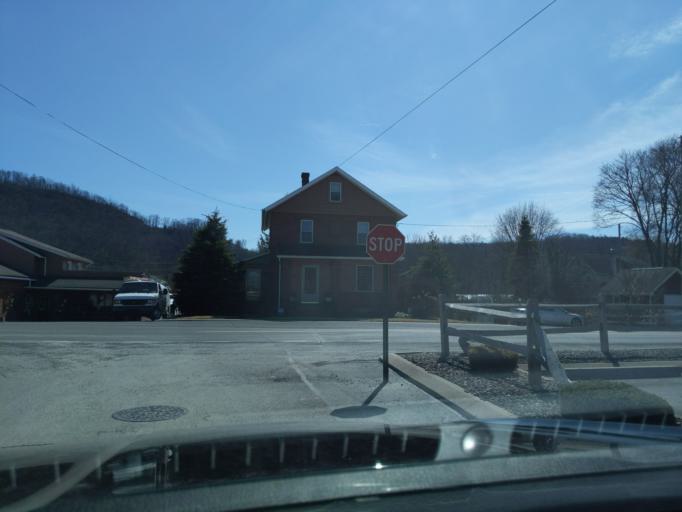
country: US
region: Pennsylvania
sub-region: Blair County
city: Hollidaysburg
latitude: 40.4253
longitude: -78.3919
